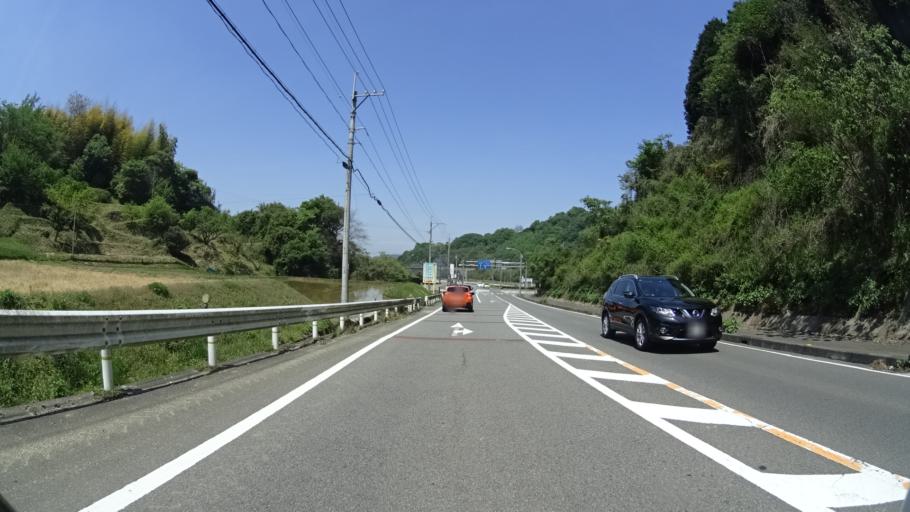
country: JP
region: Ehime
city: Hojo
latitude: 34.0011
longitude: 132.9371
